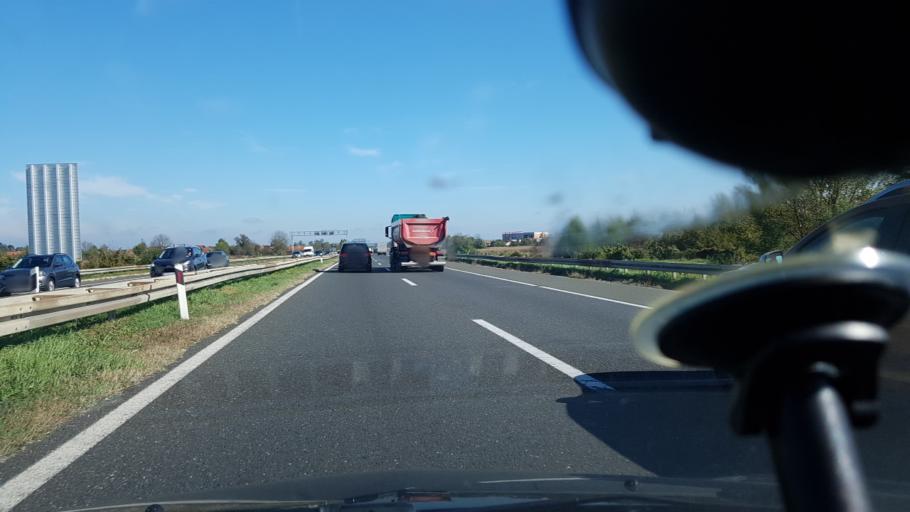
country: HR
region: Zagrebacka
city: Micevec
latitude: 45.7725
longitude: 16.1010
